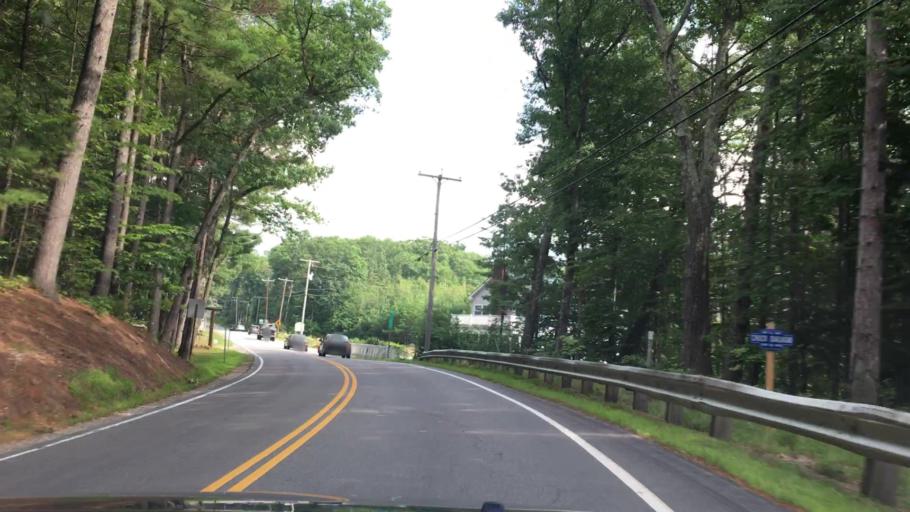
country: US
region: New Hampshire
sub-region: Belknap County
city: Gilford
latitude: 43.5957
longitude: -71.4306
